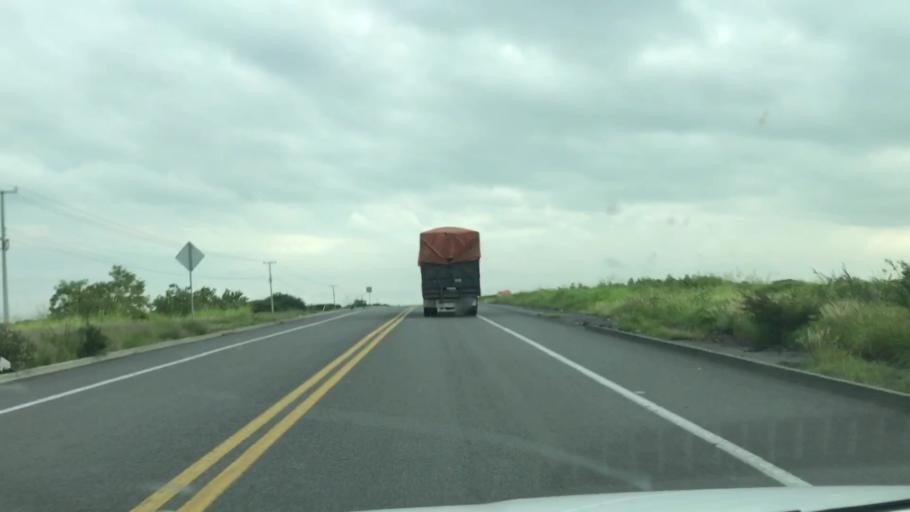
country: MX
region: Michoacan
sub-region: Yurecuaro
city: Yurecuaro
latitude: 20.3418
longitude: -102.1688
